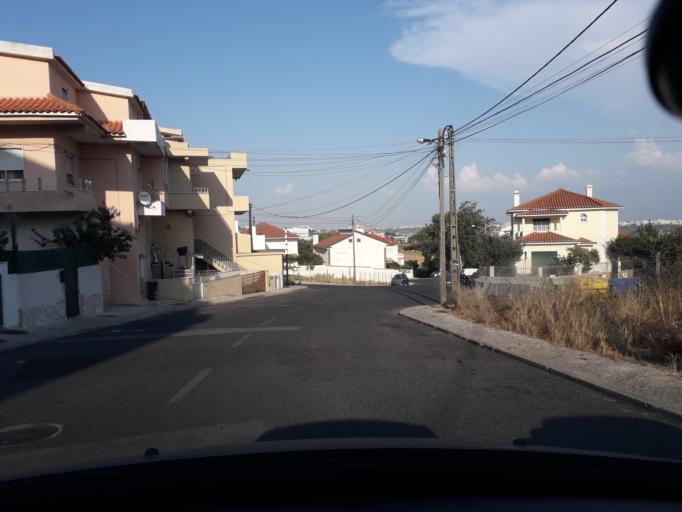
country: PT
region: Lisbon
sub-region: Odivelas
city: Famoes
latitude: 38.7883
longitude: -9.2198
